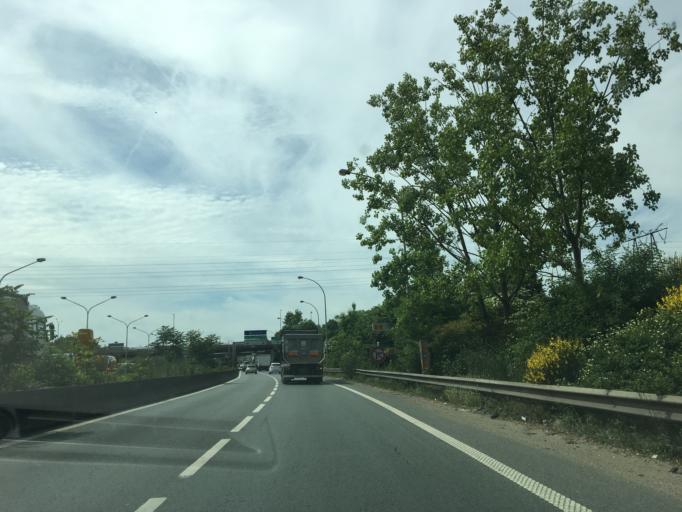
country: FR
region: Ile-de-France
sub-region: Departement du Val-de-Marne
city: Rungis
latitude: 48.7539
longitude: 2.3715
